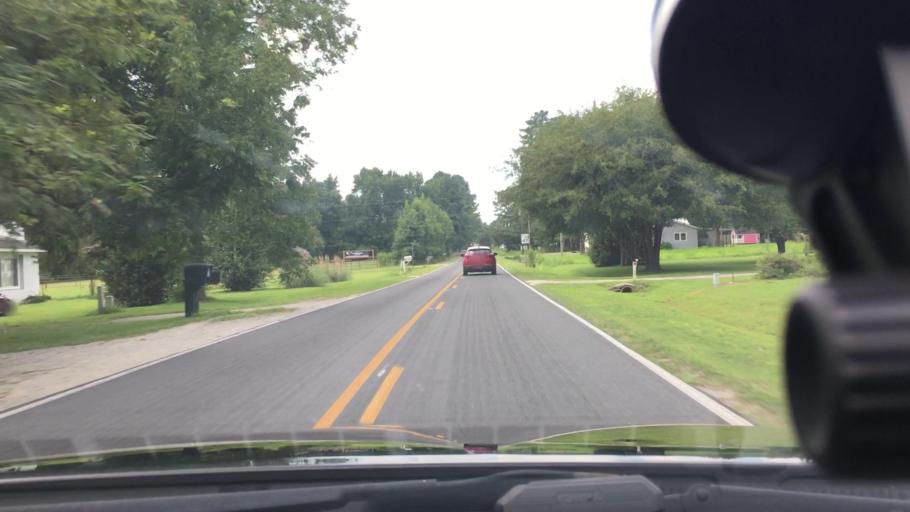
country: US
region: North Carolina
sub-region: Craven County
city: New Bern
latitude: 35.1694
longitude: -77.0505
